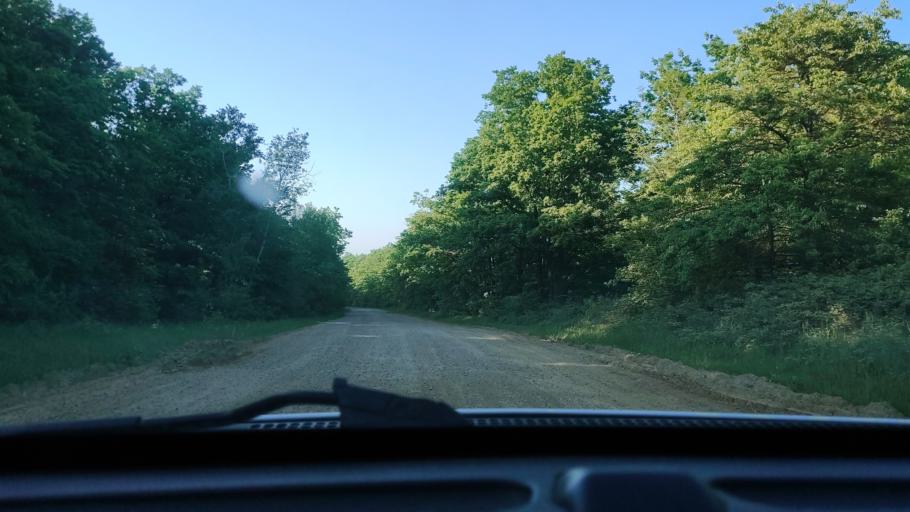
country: RU
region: Krasnodarskiy
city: Goryachiy Klyuch
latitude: 44.7080
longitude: 38.9923
